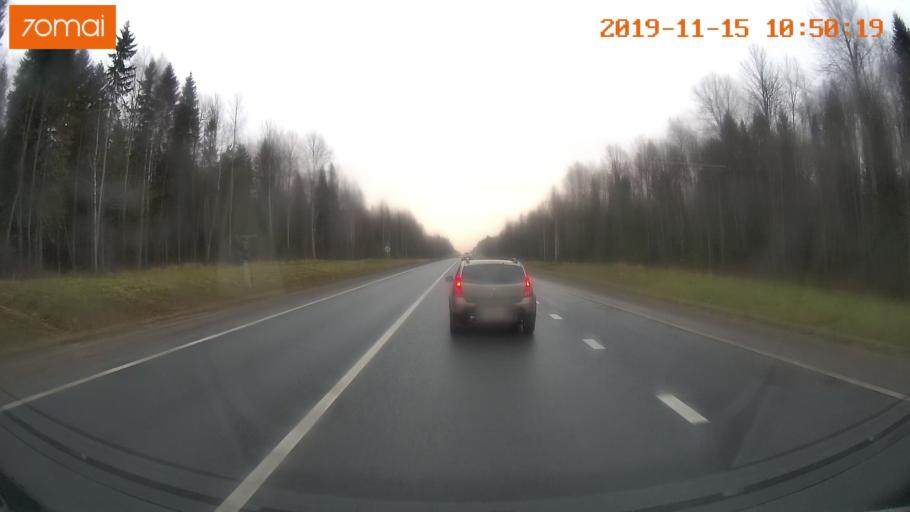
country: RU
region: Vologda
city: Chebsara
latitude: 59.1859
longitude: 38.6789
